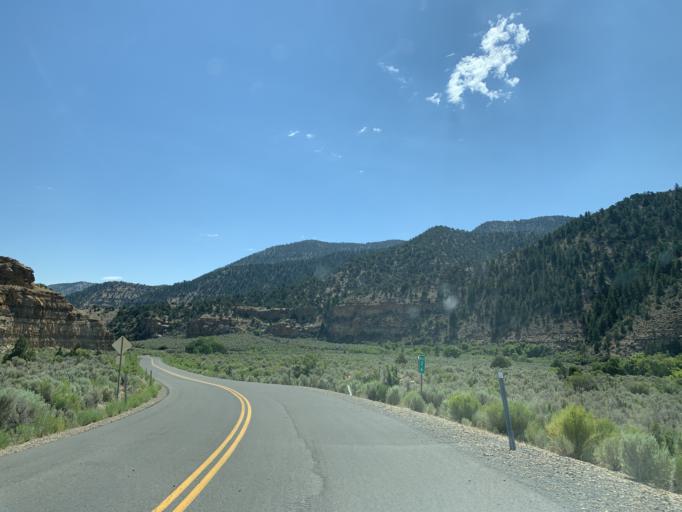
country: US
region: Utah
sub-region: Carbon County
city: East Carbon City
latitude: 39.7774
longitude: -110.4359
